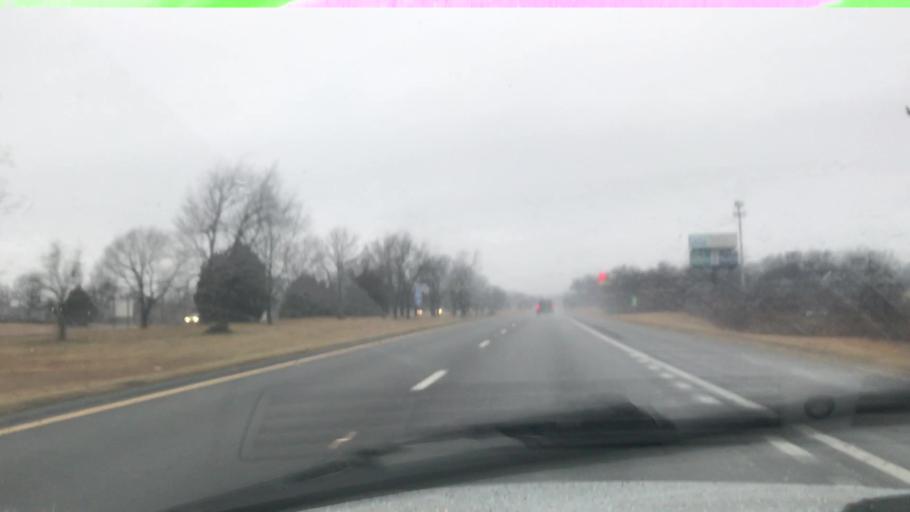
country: US
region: Tennessee
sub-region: Montgomery County
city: Clarksville
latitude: 36.6336
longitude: -87.3248
